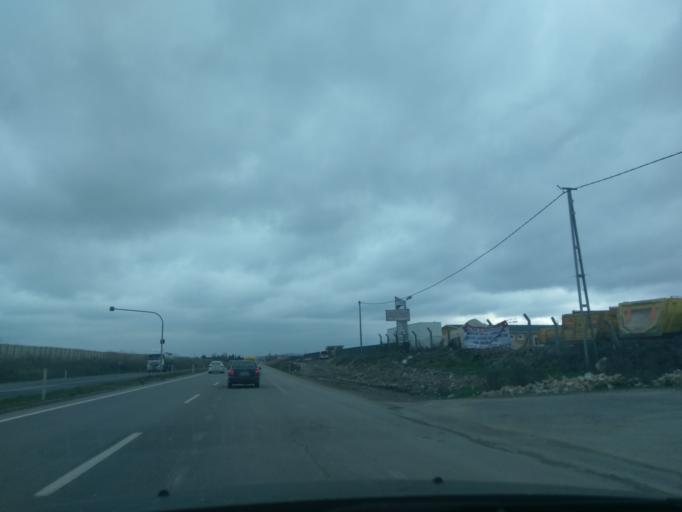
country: TR
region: Istanbul
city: Muratbey
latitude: 41.1062
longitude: 28.5059
